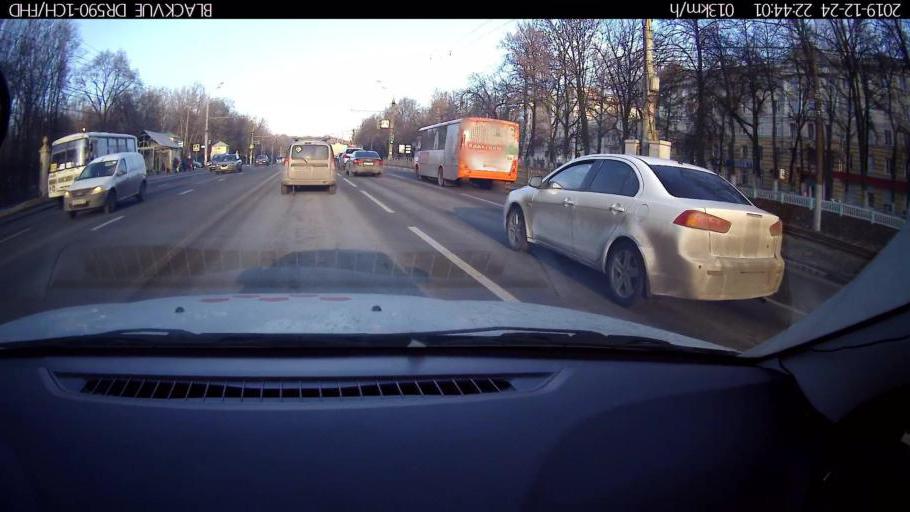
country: RU
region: Nizjnij Novgorod
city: Nizhniy Novgorod
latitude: 56.2707
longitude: 43.9761
